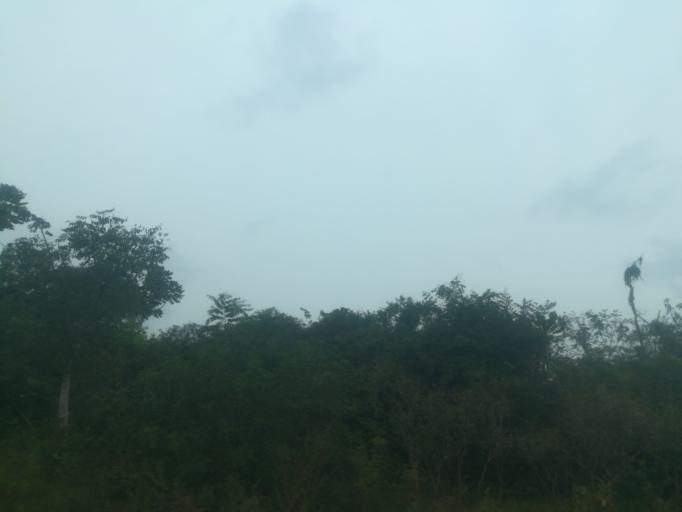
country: NG
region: Ogun
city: Ayetoro
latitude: 7.0991
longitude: 3.1265
